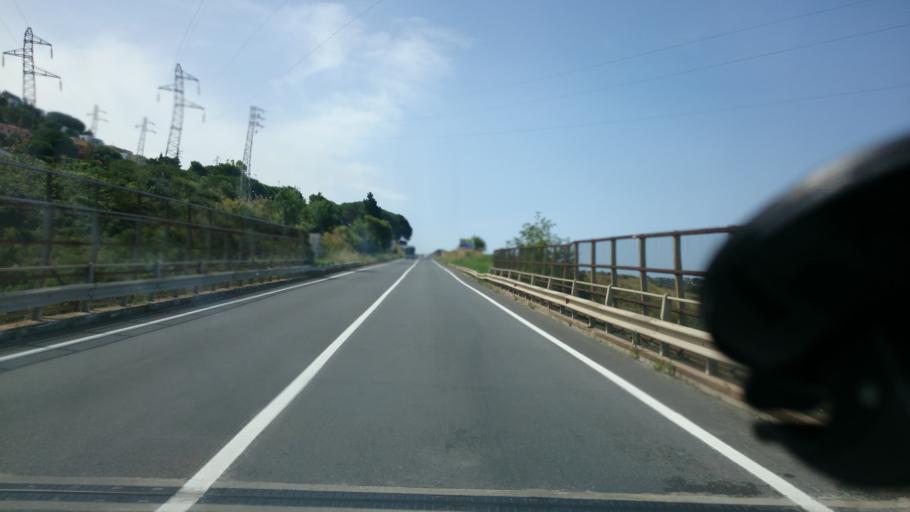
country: IT
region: Calabria
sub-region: Provincia di Cosenza
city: San Nicola Arcella
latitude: 39.8676
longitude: 15.7964
